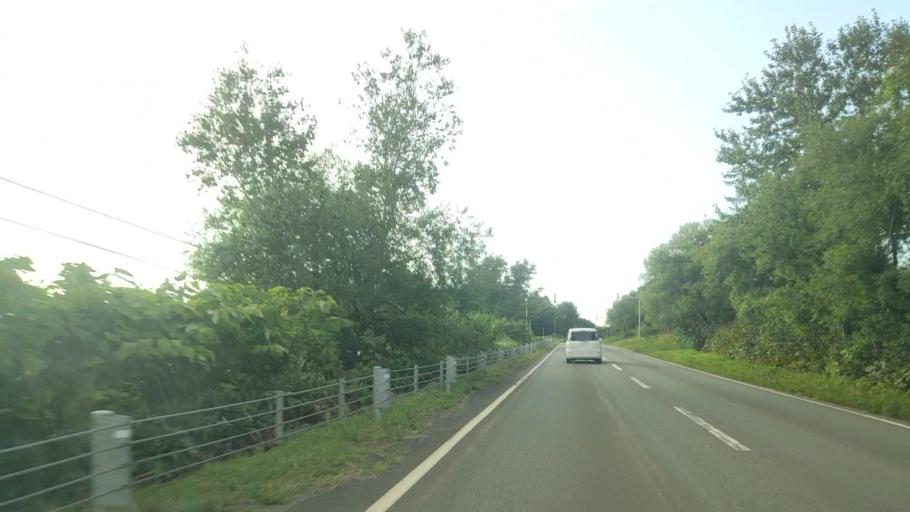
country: JP
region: Hokkaido
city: Makubetsu
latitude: 45.0454
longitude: 141.7535
